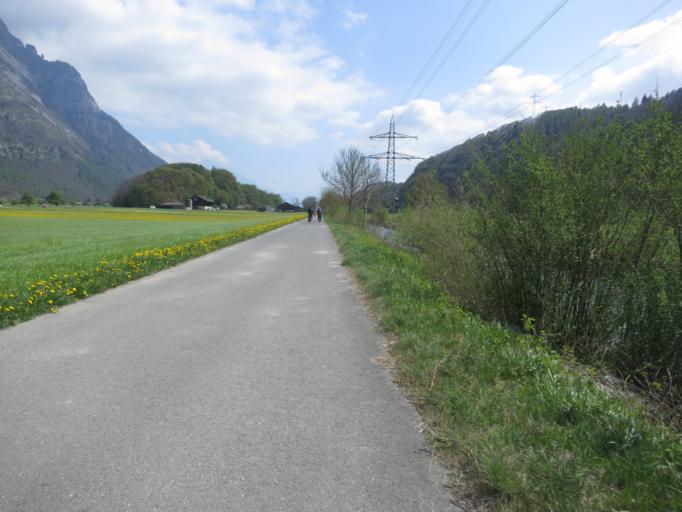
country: CH
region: Saint Gallen
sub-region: Wahlkreis Sarganserland
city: Flums
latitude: 47.0666
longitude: 9.3829
